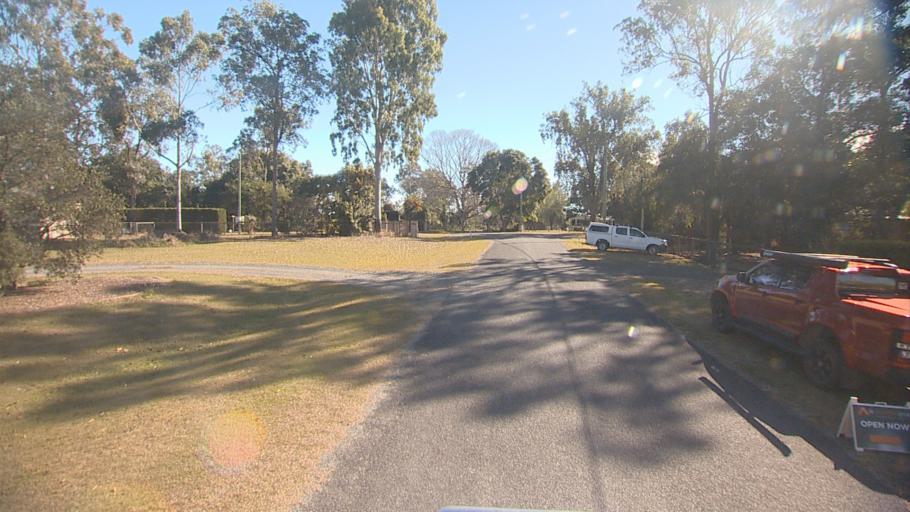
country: AU
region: Queensland
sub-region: Logan
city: Chambers Flat
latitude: -27.7738
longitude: 153.0789
